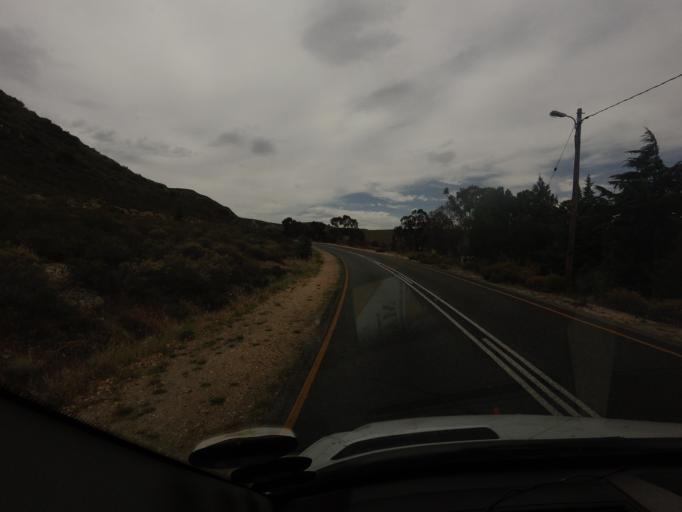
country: ZA
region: Western Cape
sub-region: Overberg District Municipality
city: Swellendam
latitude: -33.9001
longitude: 20.7231
